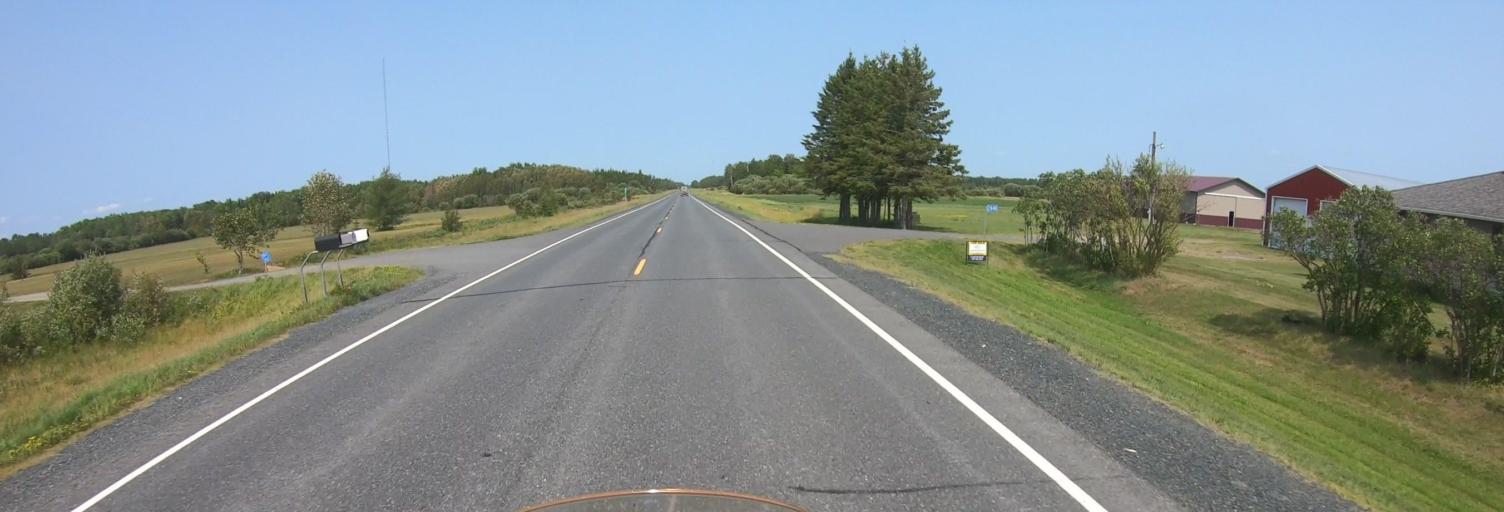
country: US
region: Minnesota
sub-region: Koochiching County
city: International Falls
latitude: 48.5532
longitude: -93.8183
